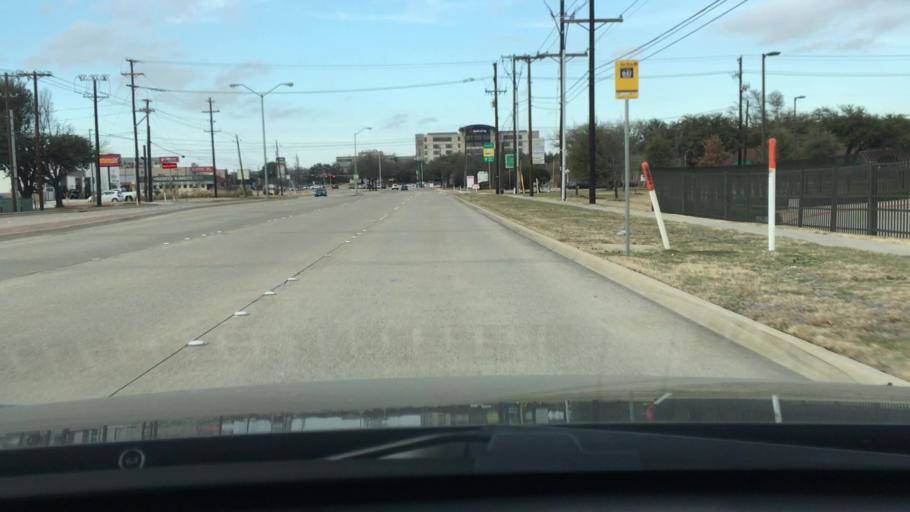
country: US
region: Texas
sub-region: Collin County
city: Plano
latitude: 33.0155
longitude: -96.7666
